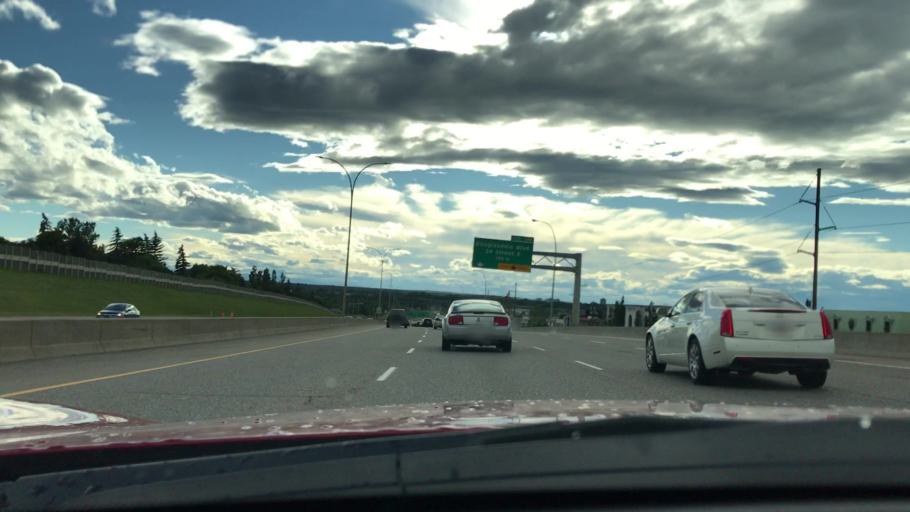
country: CA
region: Alberta
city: Calgary
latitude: 50.9469
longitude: -113.9883
